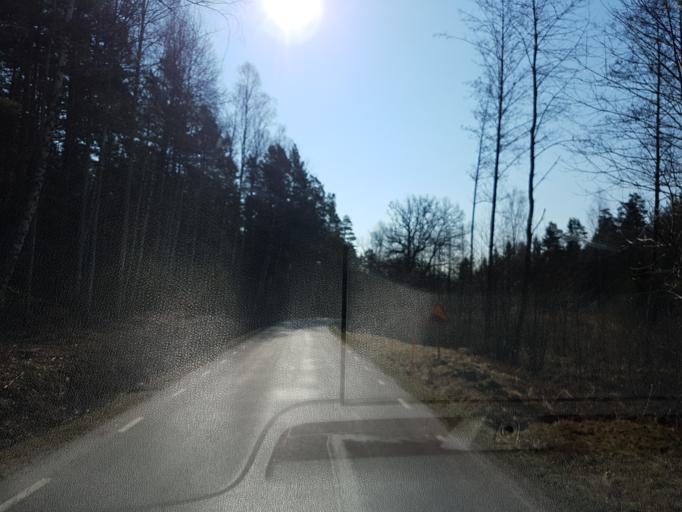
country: SE
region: Kalmar
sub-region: Vasterviks Kommun
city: Overum
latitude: 58.1531
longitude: 16.2277
